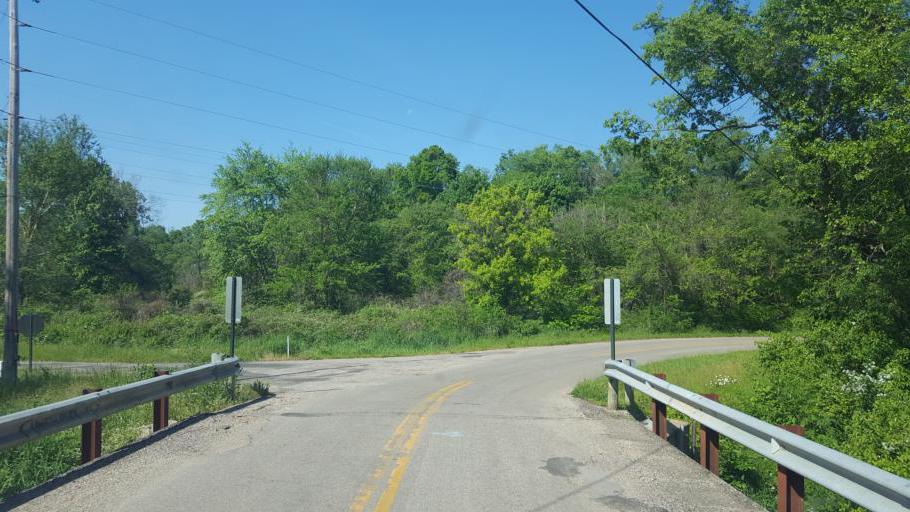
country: US
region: Ohio
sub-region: Jackson County
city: Wellston
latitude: 39.0068
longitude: -82.4700
